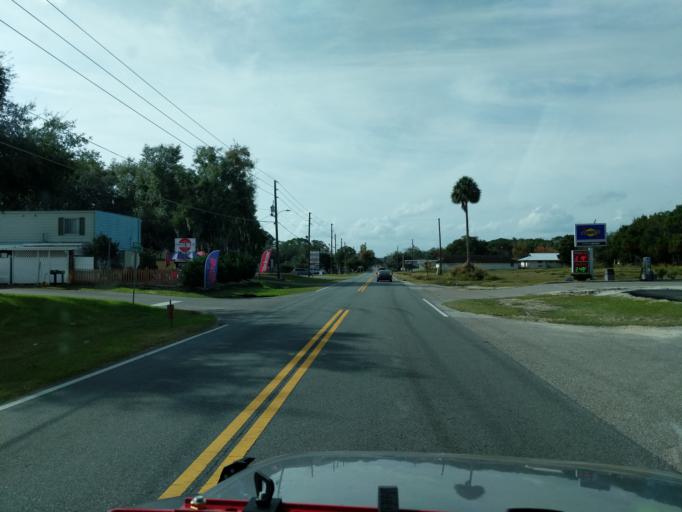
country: US
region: Florida
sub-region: Lake County
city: Tavares
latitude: 28.8041
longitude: -81.7163
